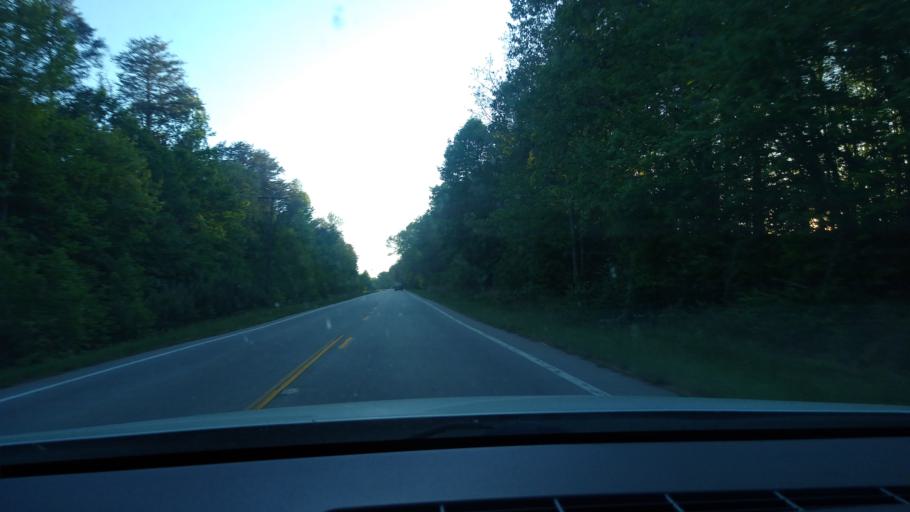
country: US
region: North Carolina
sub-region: Rockingham County
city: Reidsville
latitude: 36.3975
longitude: -79.5387
